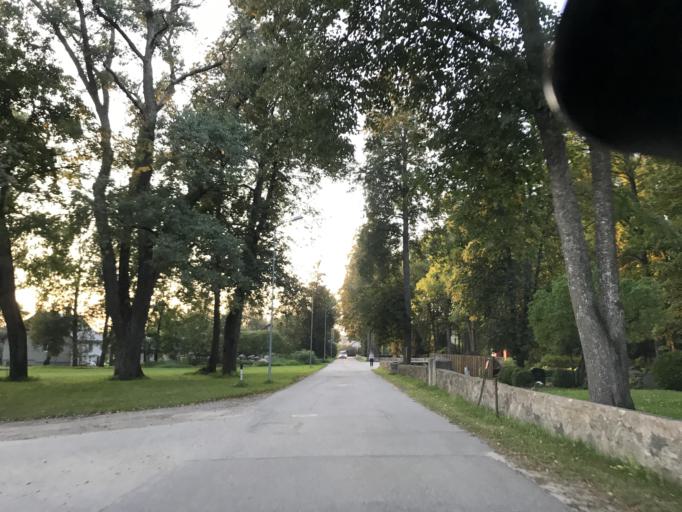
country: LV
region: Ikskile
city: Ikskile
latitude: 56.8310
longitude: 24.4946
